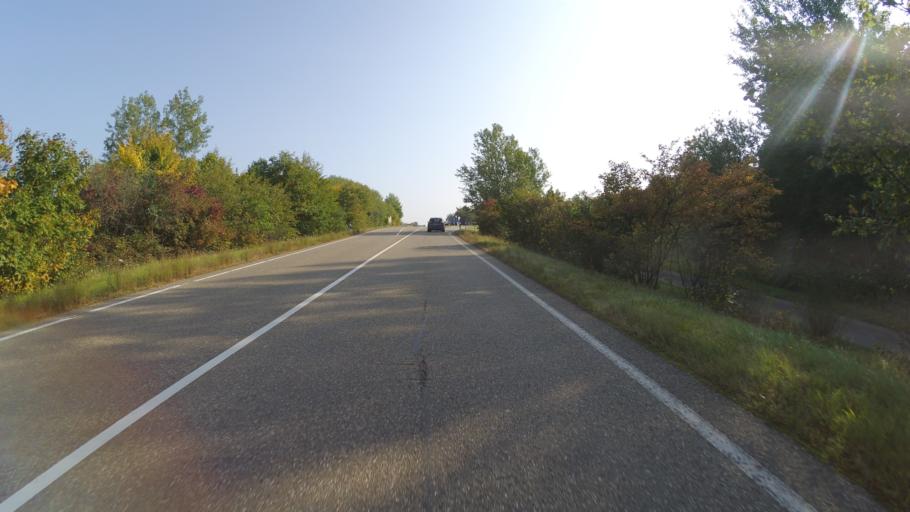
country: DE
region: Rheinland-Pfalz
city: Landstuhl
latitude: 49.3964
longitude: 7.5512
